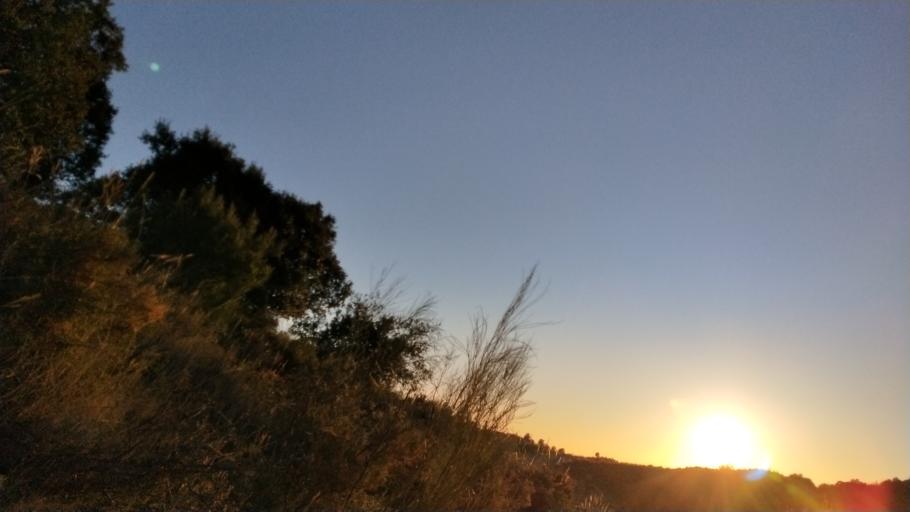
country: ES
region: Andalusia
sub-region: Provincia de Granada
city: Beas de Granada
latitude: 37.2050
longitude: -3.4988
